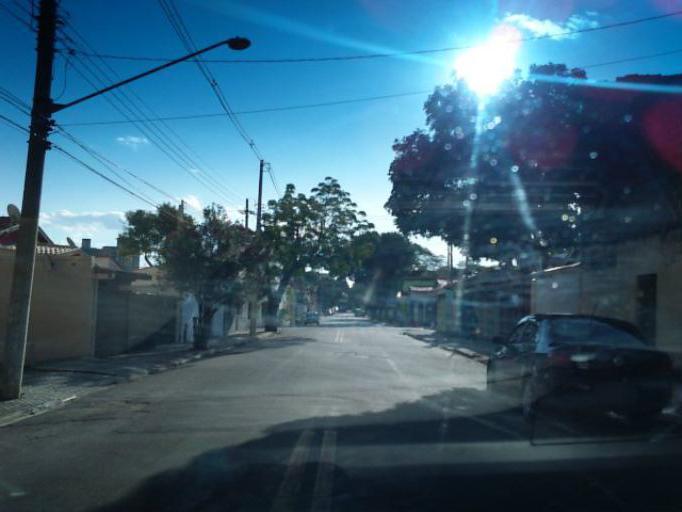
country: BR
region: Sao Paulo
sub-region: Sao Jose Dos Campos
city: Sao Jose dos Campos
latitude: -23.1758
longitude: -45.8865
